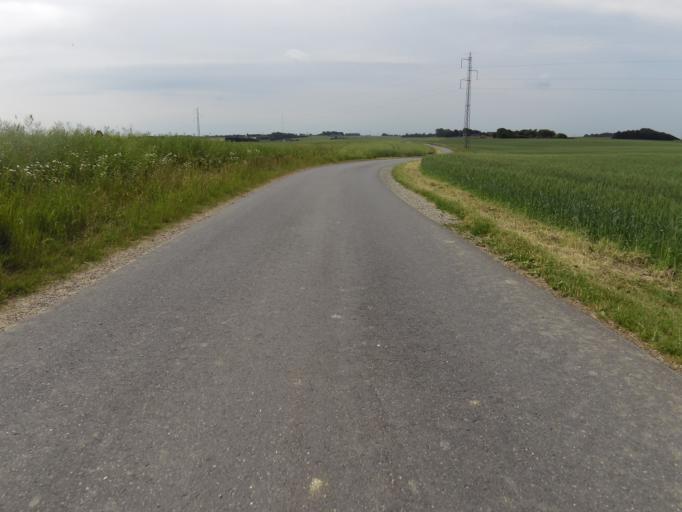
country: DK
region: Central Jutland
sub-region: Holstebro Kommune
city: Holstebro
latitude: 56.4275
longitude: 8.6676
